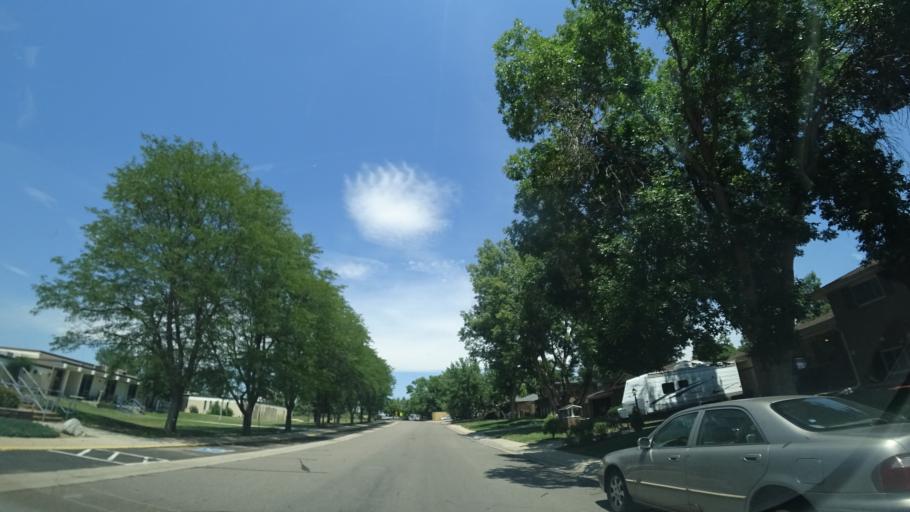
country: US
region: Colorado
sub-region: Jefferson County
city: Lakewood
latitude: 39.6932
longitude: -105.0955
